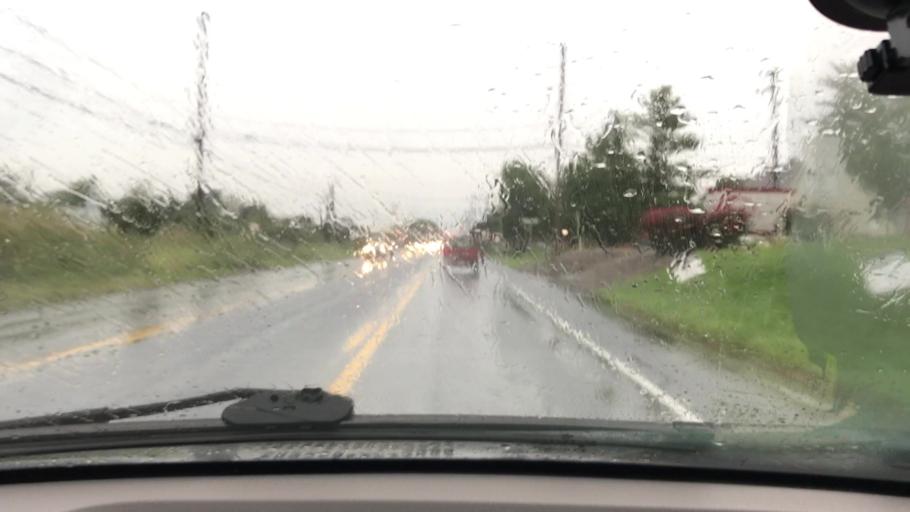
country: US
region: Pennsylvania
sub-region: Lancaster County
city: Rheems
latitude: 40.1327
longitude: -76.5684
